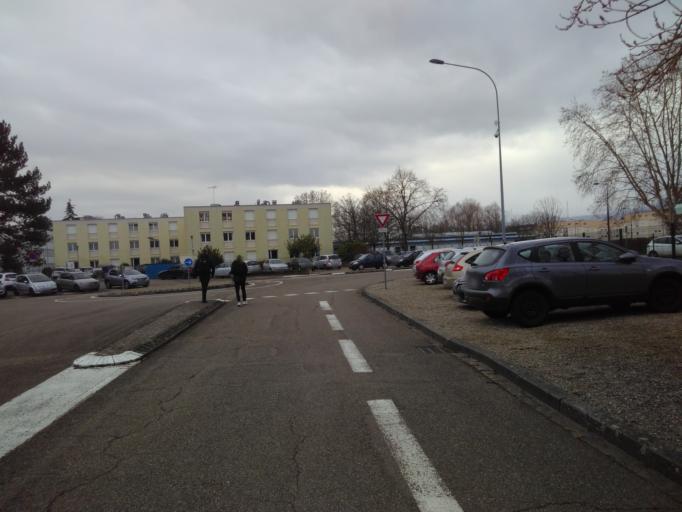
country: FR
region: Alsace
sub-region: Departement du Bas-Rhin
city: Selestat
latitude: 48.2540
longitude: 7.4491
